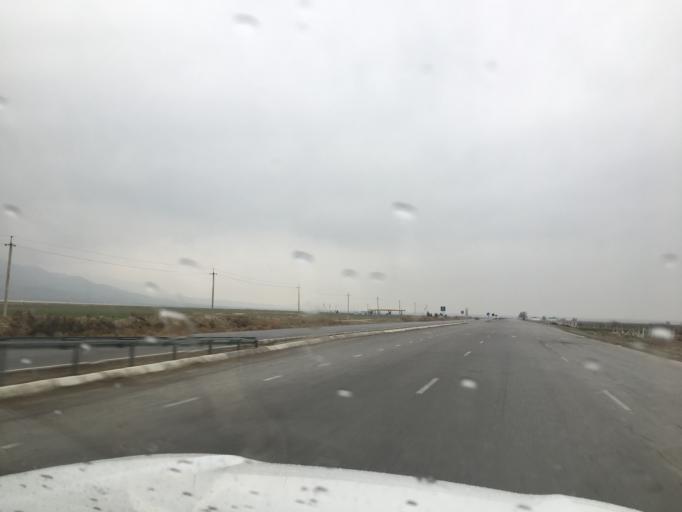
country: TM
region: Ahal
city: Annau
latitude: 37.7915
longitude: 58.8234
